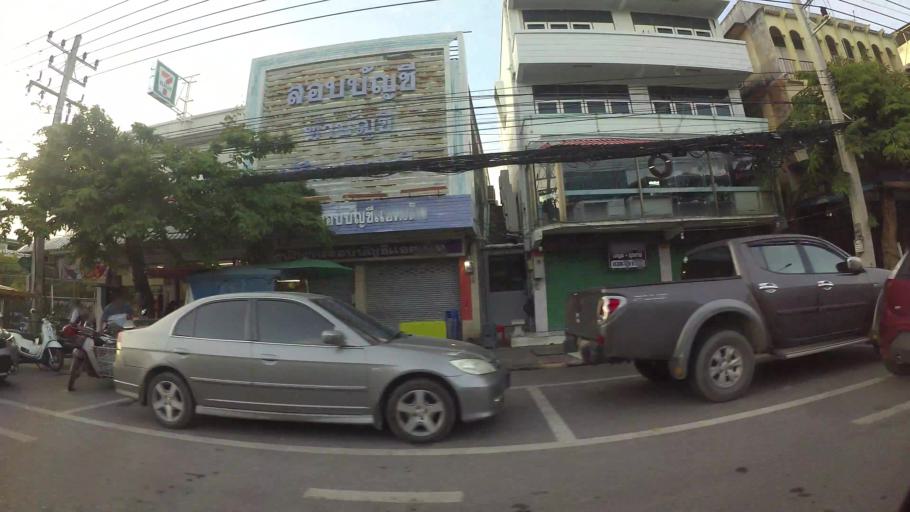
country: TH
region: Rayong
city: Rayong
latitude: 12.6817
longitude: 101.2785
